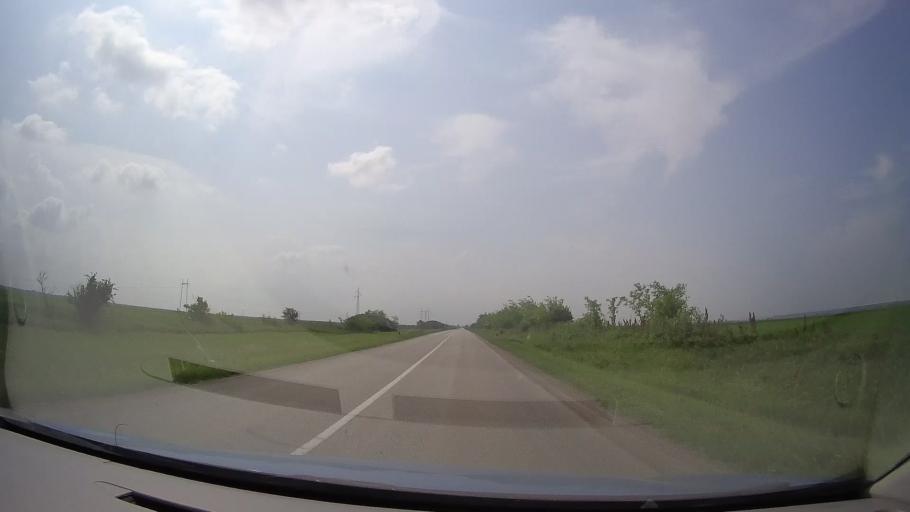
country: RS
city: Crepaja
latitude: 44.9727
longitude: 20.6490
